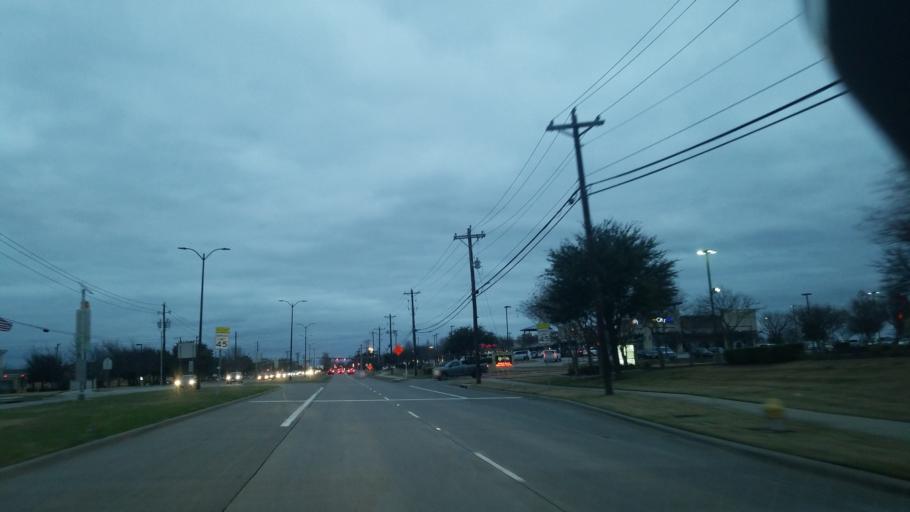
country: US
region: Texas
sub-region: Collin County
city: Frisco
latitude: 33.1225
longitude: -96.8084
